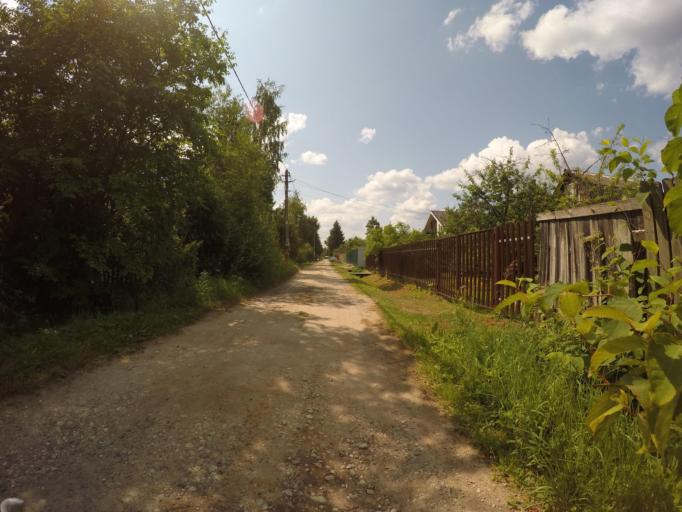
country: RU
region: Moskovskaya
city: Rechitsy
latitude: 55.6100
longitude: 38.4981
